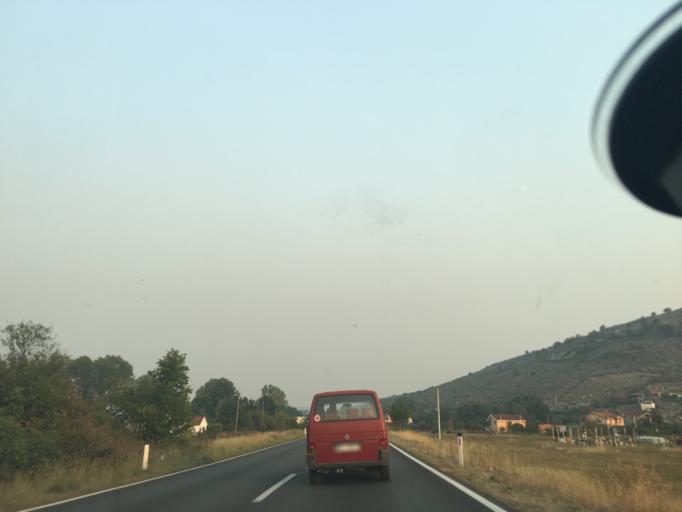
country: ME
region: Danilovgrad
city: Danilovgrad
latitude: 42.5108
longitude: 19.1298
